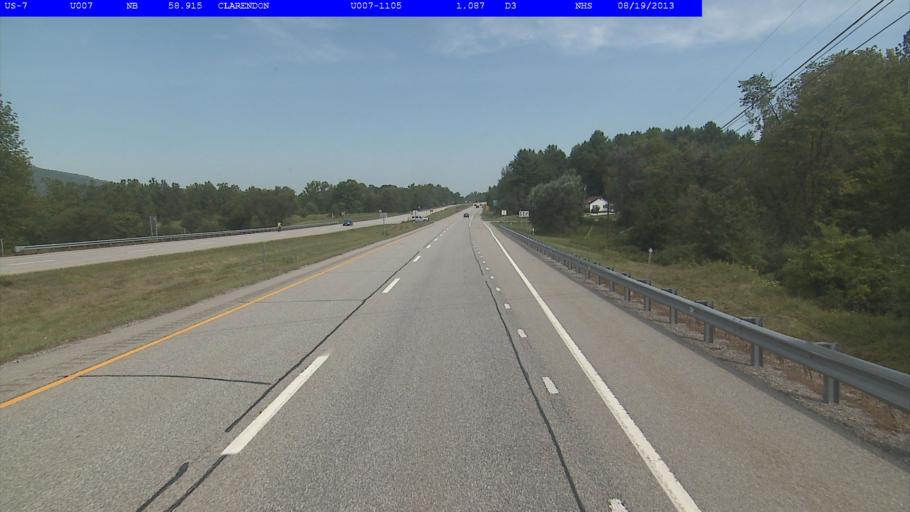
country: US
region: Vermont
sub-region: Rutland County
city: Rutland
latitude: 43.5102
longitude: -72.9672
